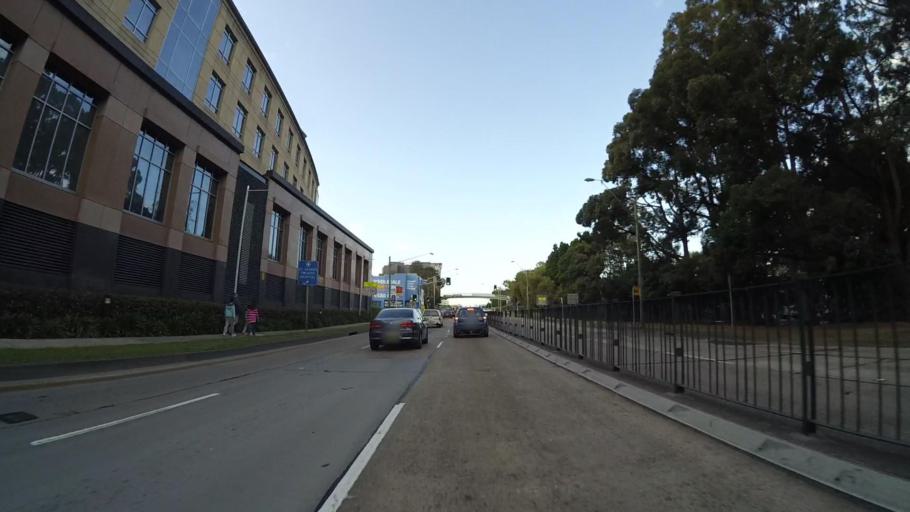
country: AU
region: New South Wales
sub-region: Kogarah
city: Beverly Park
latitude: -33.9669
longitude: 151.1366
